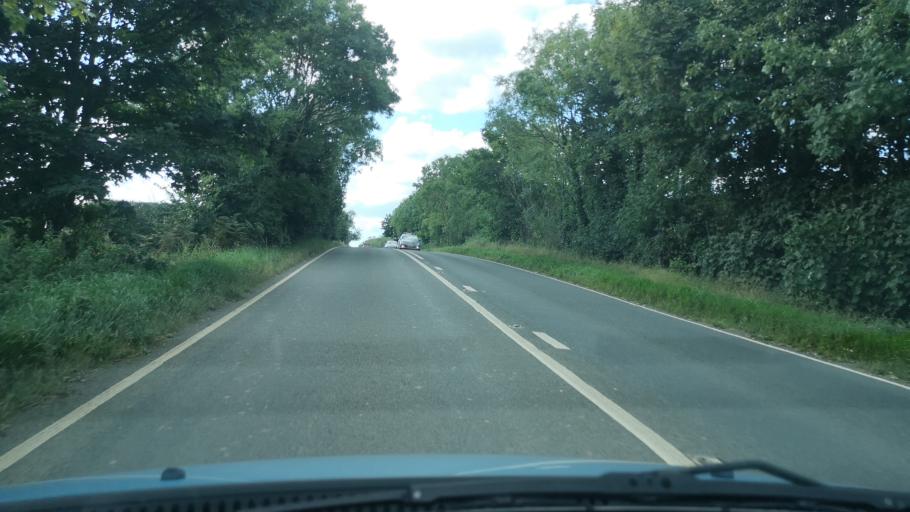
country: GB
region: England
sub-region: City and Borough of Wakefield
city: Badsworth
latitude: 53.6162
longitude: -1.3030
